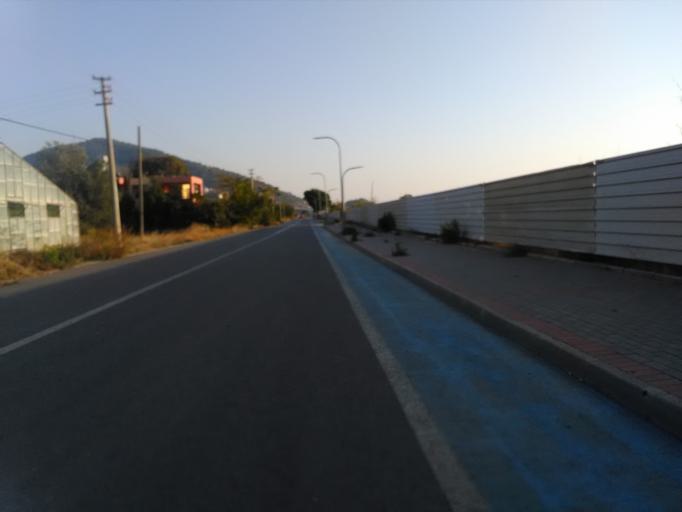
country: TR
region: Antalya
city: Gazipasa
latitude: 36.2528
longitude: 32.2918
